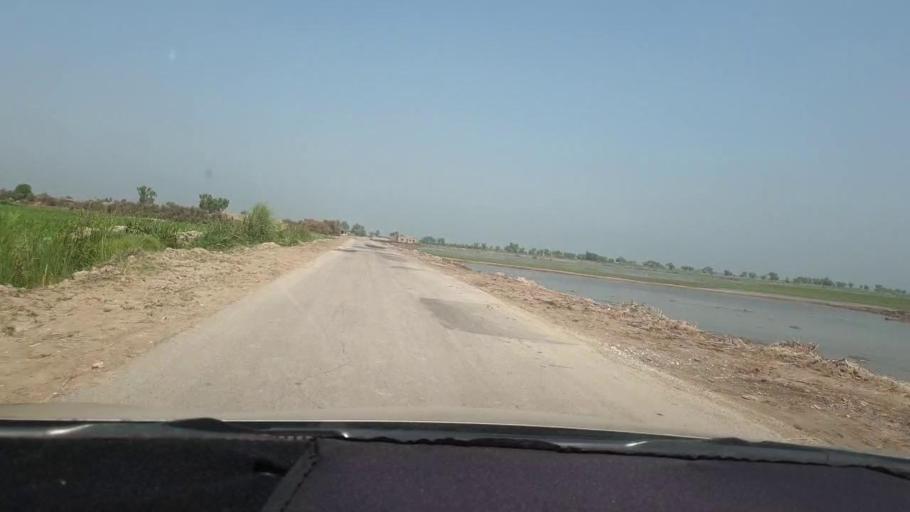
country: PK
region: Sindh
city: Miro Khan
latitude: 27.8143
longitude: 68.0285
